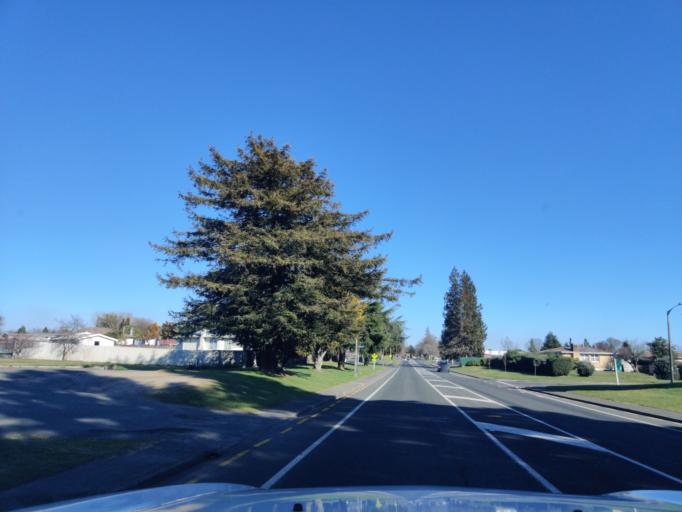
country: NZ
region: Waikato
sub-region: South Waikato District
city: Tokoroa
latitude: -38.2285
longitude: 175.8659
